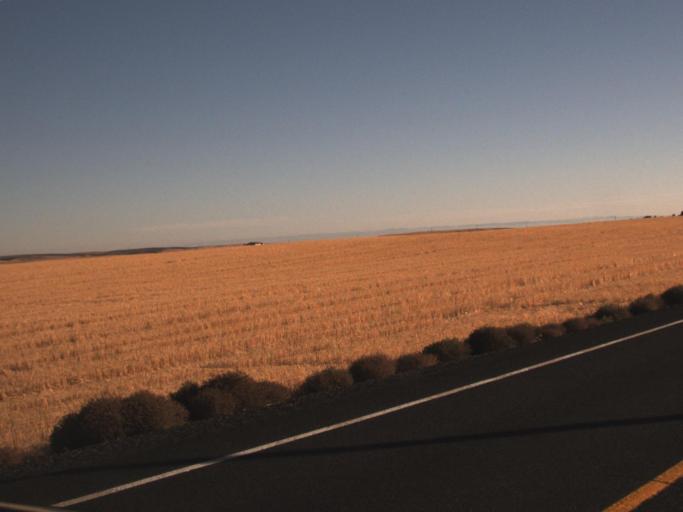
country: US
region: Washington
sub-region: Adams County
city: Ritzville
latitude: 46.8926
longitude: -118.3338
